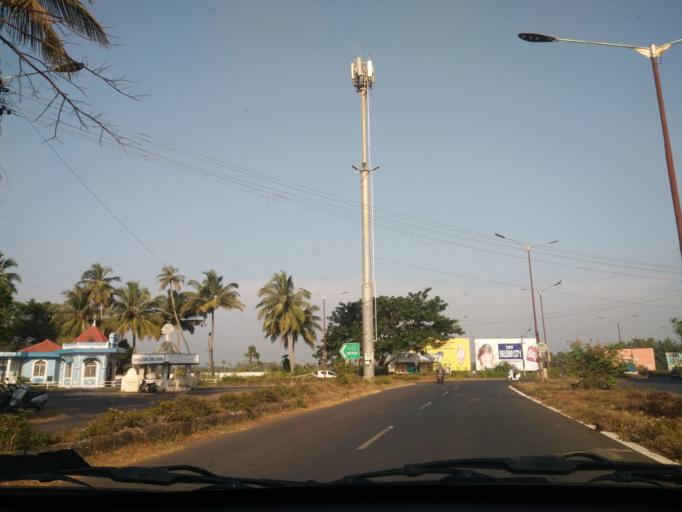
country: IN
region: Goa
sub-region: South Goa
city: Chinchinim
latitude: 15.2187
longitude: 73.9788
